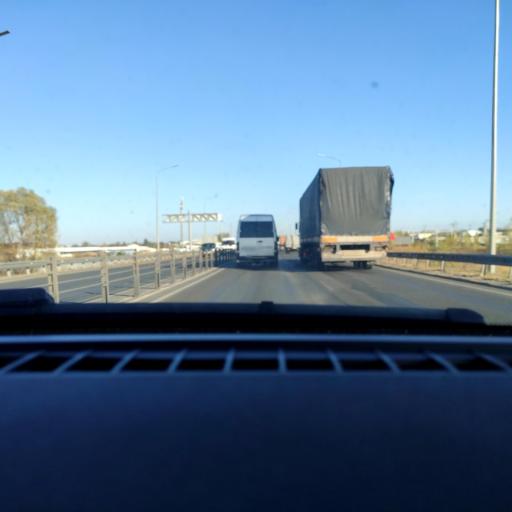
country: RU
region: Voronezj
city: Somovo
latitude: 51.6776
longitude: 39.3080
